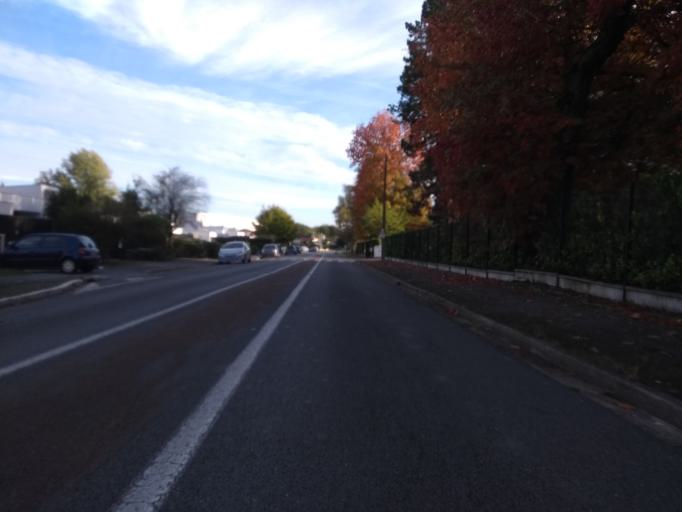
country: FR
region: Aquitaine
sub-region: Departement de la Gironde
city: Pessac
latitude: 44.7909
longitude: -0.6402
